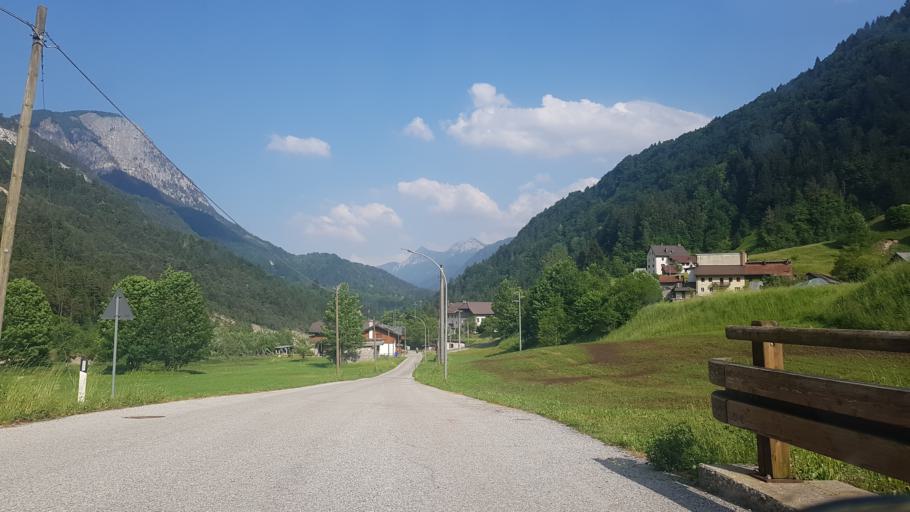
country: IT
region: Friuli Venezia Giulia
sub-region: Provincia di Udine
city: Pontebba
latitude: 46.5215
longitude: 13.2707
